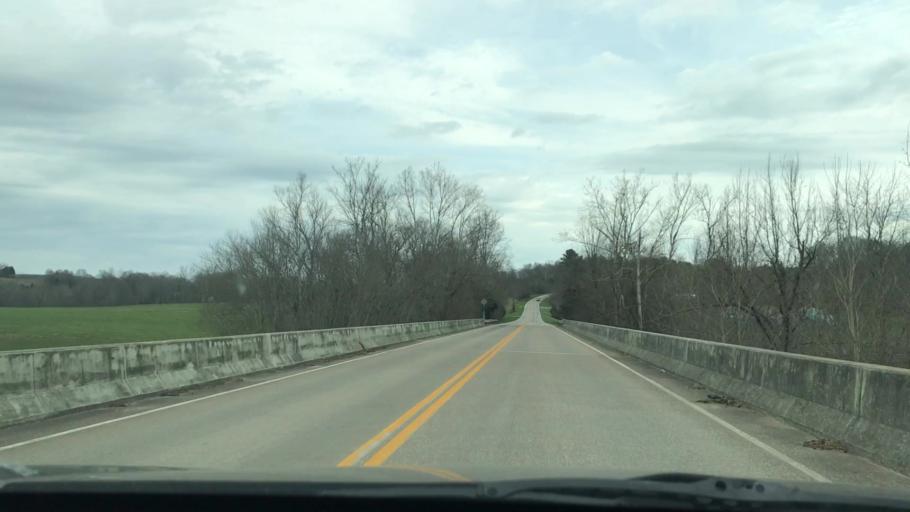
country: US
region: Kentucky
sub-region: Hart County
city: Munfordville
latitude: 37.3190
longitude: -85.7636
